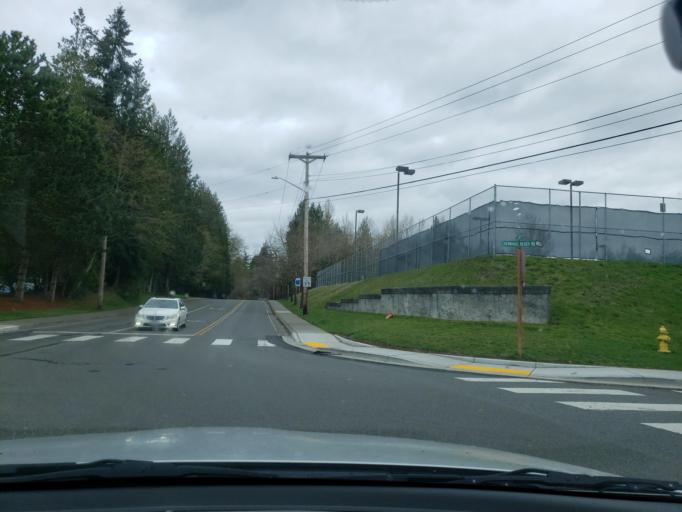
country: US
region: Washington
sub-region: Snohomish County
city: Mukilteo
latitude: 47.8950
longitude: -122.3004
